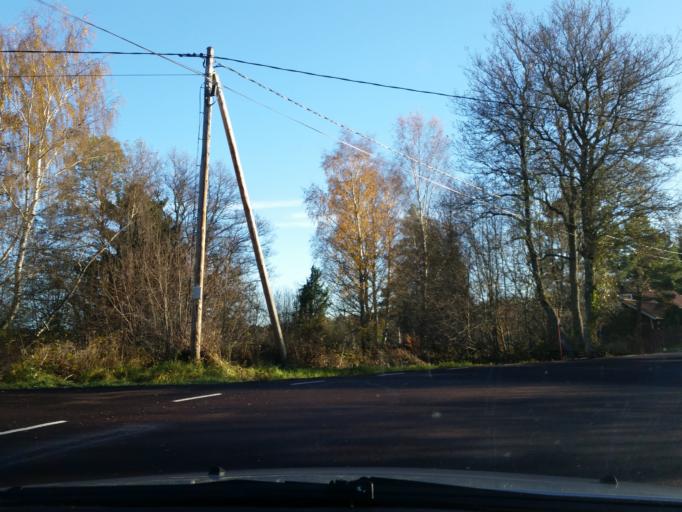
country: AX
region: Alands landsbygd
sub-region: Jomala
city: Jomala
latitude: 60.2010
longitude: 19.9572
